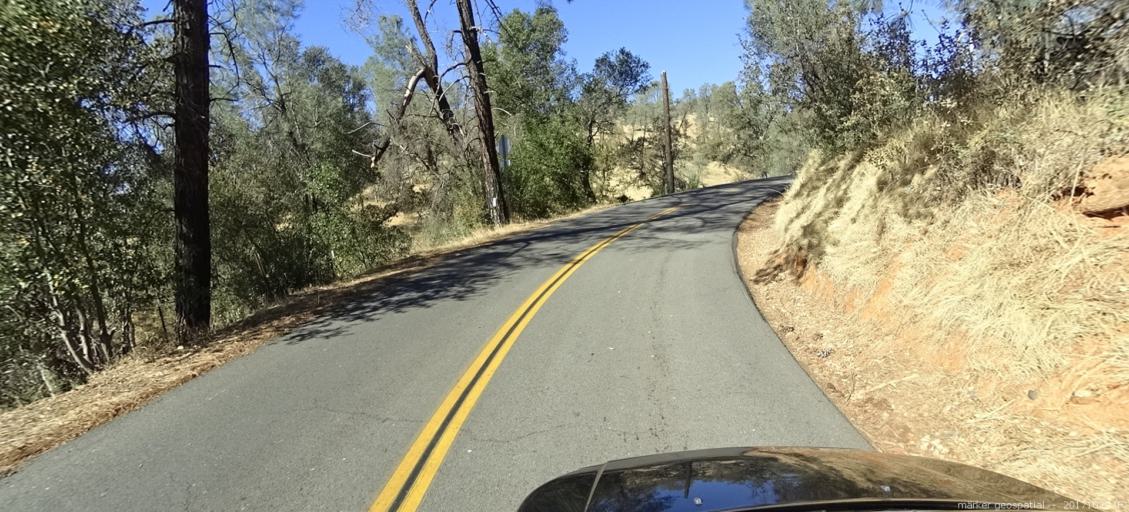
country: US
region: California
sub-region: Shasta County
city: Shasta
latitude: 40.4773
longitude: -122.6291
